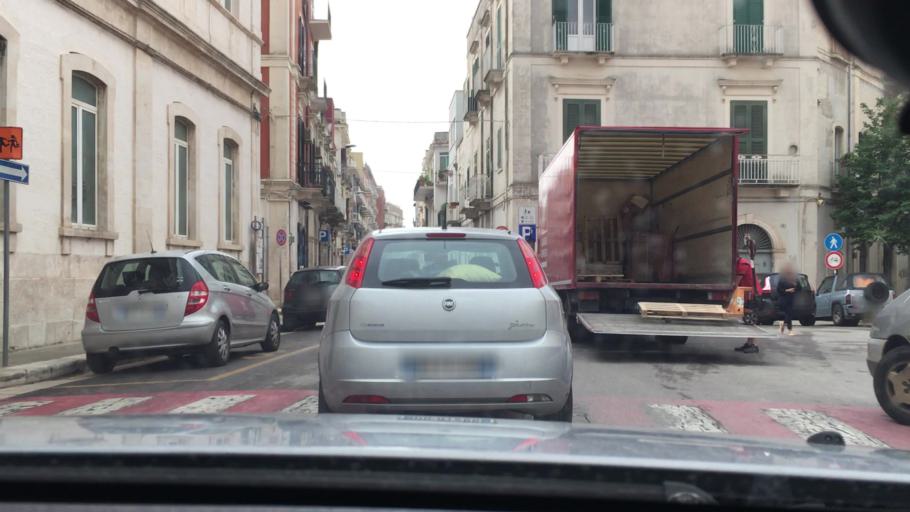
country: IT
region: Apulia
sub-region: Provincia di Bari
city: Gioia del Colle
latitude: 40.7980
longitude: 16.9209
